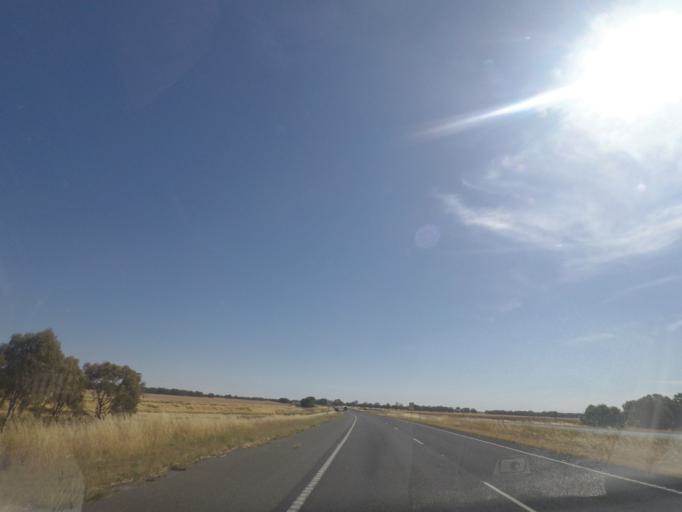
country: AU
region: Victoria
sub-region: Greater Shepparton
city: Shepparton
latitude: -36.6199
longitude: 145.3059
